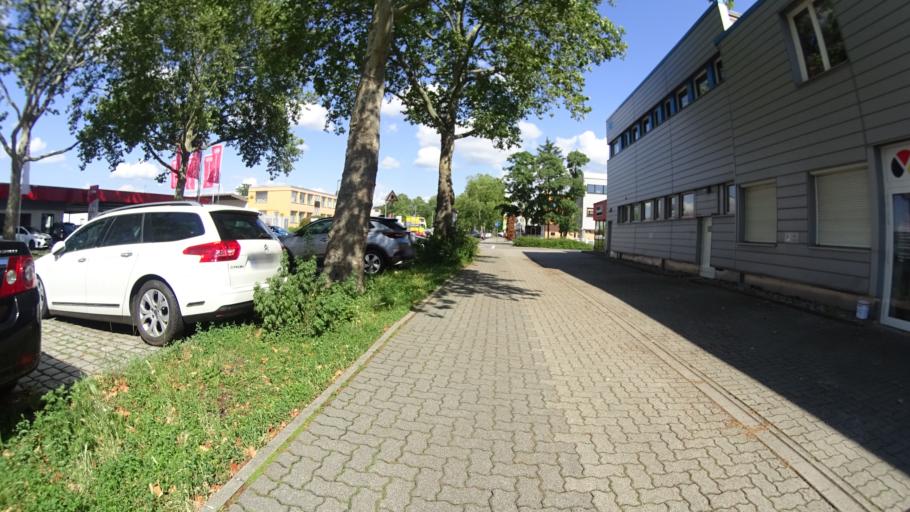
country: DE
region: Baden-Wuerttemberg
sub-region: Karlsruhe Region
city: Karlsruhe
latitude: 48.9965
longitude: 8.4446
